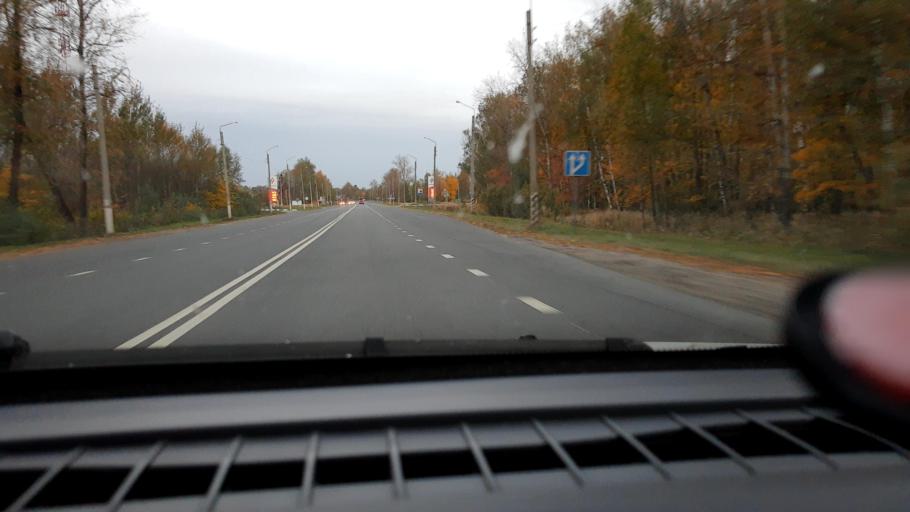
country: RU
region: Vladimir
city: Orgtrud
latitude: 56.2075
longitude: 40.6854
